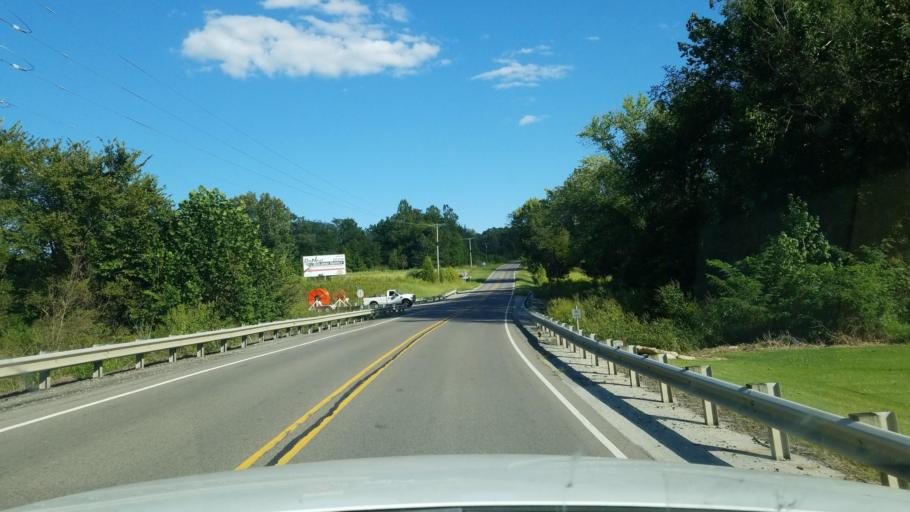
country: US
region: Illinois
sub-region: Saline County
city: Harrisburg
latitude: 37.6360
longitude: -88.4843
